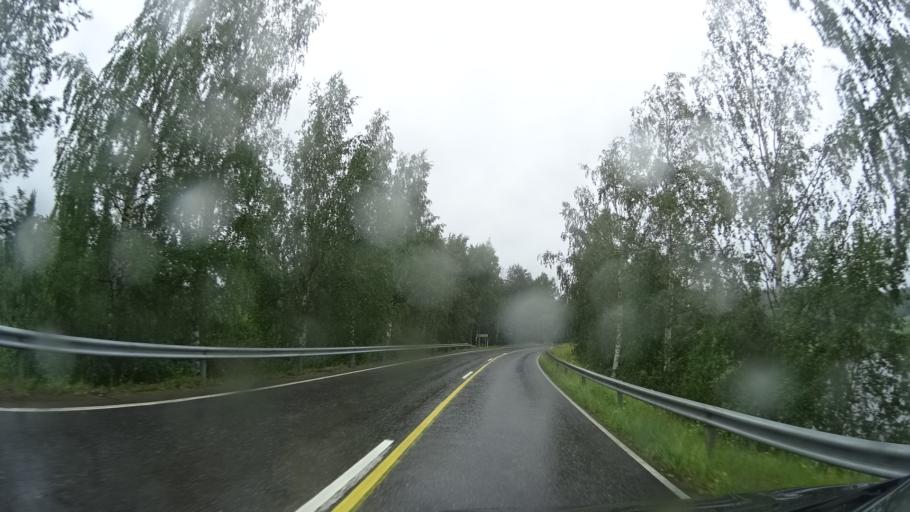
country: FI
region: North Karelia
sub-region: Keski-Karjala
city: Raeaekkylae
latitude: 62.3092
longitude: 29.5875
